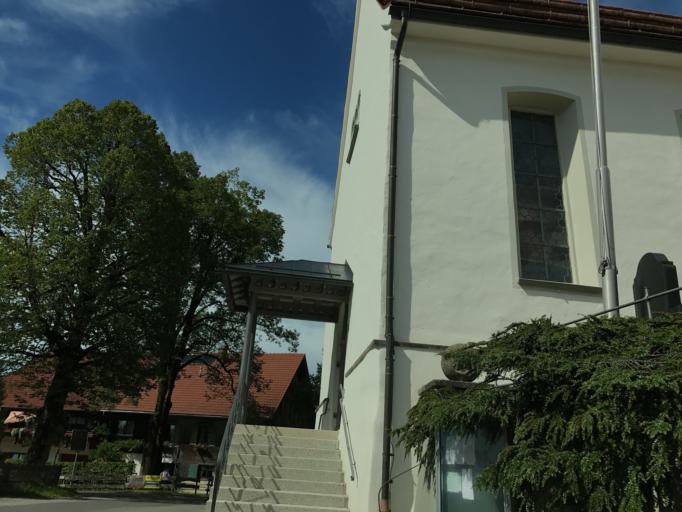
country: DE
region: Bavaria
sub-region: Swabia
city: Rothenbach
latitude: 47.6009
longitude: 9.9581
